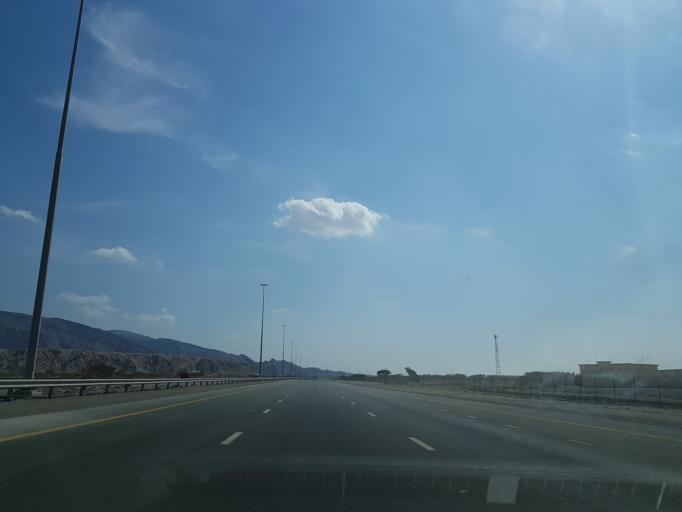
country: AE
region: Ra's al Khaymah
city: Ras al-Khaimah
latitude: 25.7925
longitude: 56.0310
